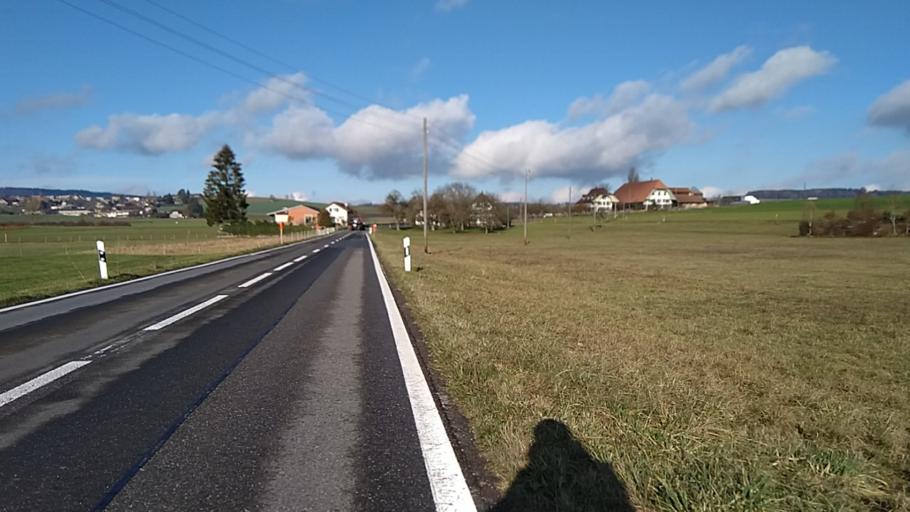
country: CH
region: Bern
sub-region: Bern-Mittelland District
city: Kirchlindach
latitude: 46.9805
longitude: 7.3997
